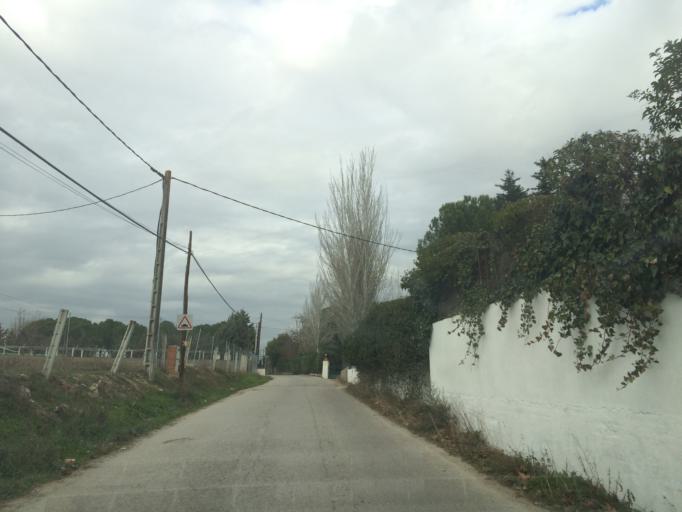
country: ES
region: Madrid
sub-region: Provincia de Madrid
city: Arroyomolinos
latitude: 40.3020
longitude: -3.9447
